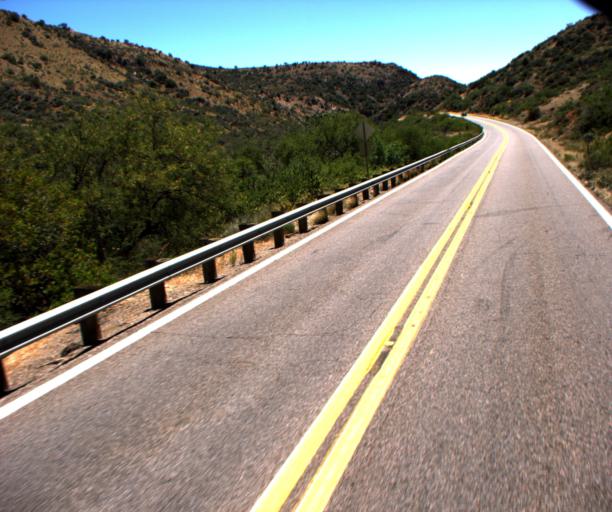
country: US
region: Arizona
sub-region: Gila County
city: Globe
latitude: 33.2144
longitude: -110.7971
